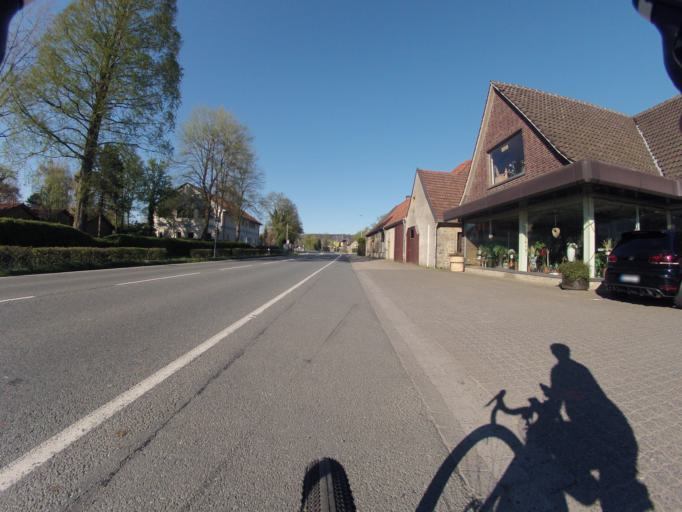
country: DE
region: North Rhine-Westphalia
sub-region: Regierungsbezirk Munster
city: Birgte
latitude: 52.2309
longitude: 7.6896
